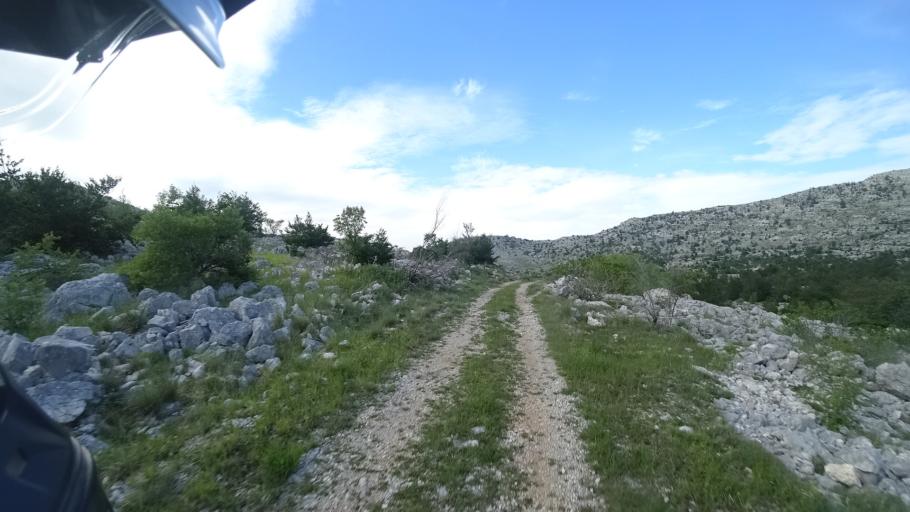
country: HR
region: Splitsko-Dalmatinska
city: Hrvace
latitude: 43.8041
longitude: 16.4330
